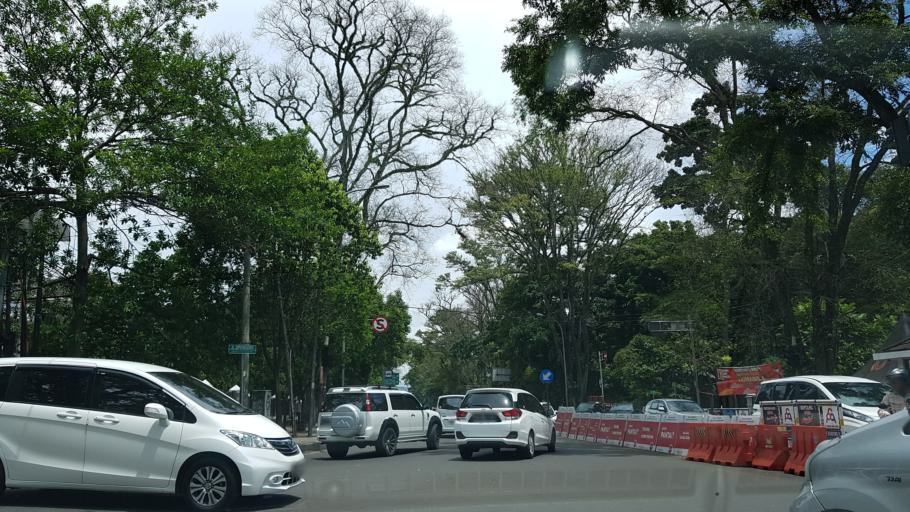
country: ID
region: West Java
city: Bandung
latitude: -6.9012
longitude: 107.6192
